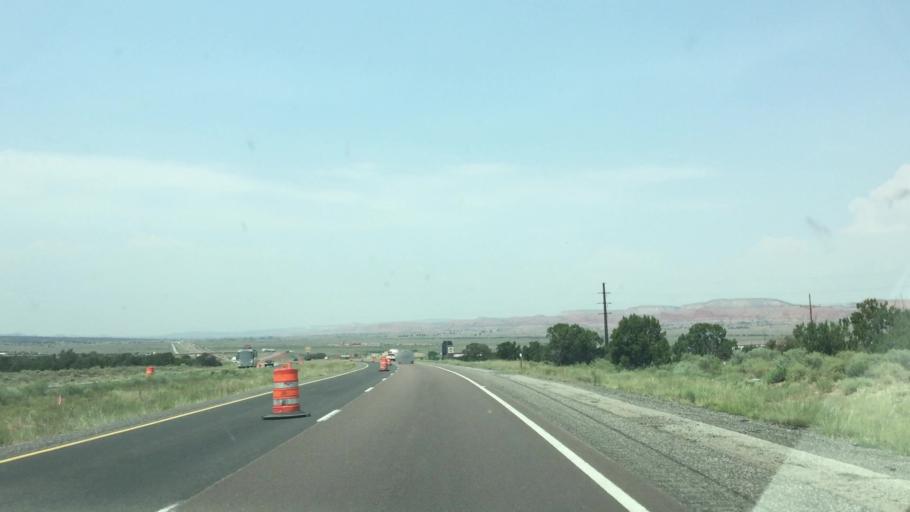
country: US
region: New Mexico
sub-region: McKinley County
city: Church Rock
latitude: 35.4771
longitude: -108.4241
